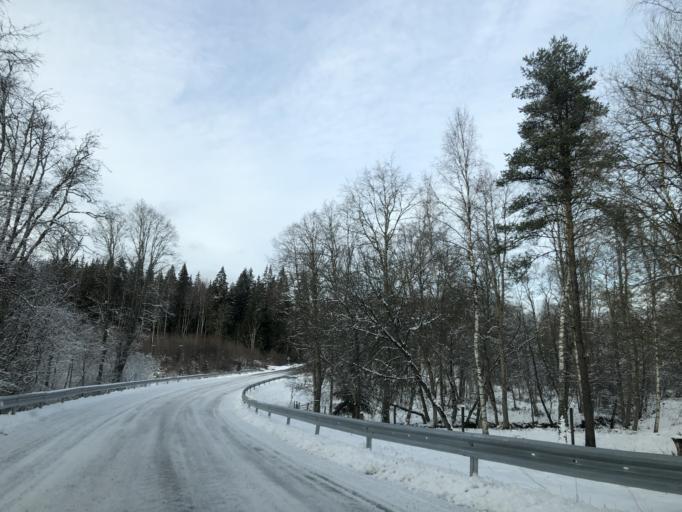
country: SE
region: Vaestra Goetaland
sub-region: Ulricehamns Kommun
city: Ulricehamn
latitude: 57.8061
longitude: 13.5450
